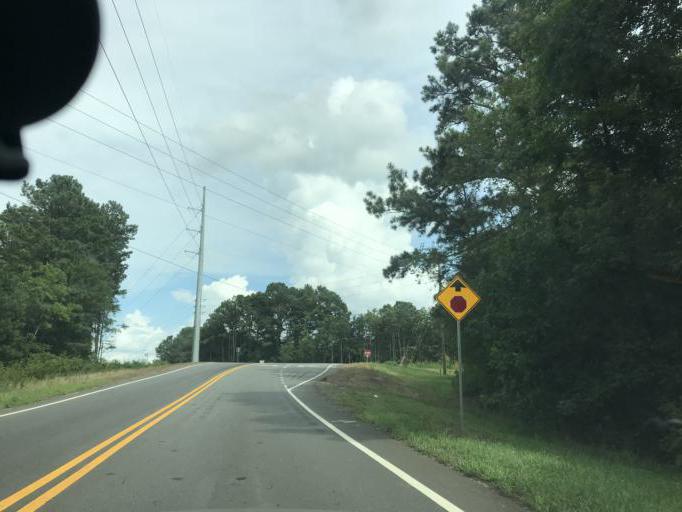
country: US
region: Georgia
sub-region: Forsyth County
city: Cumming
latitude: 34.3068
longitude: -84.2162
